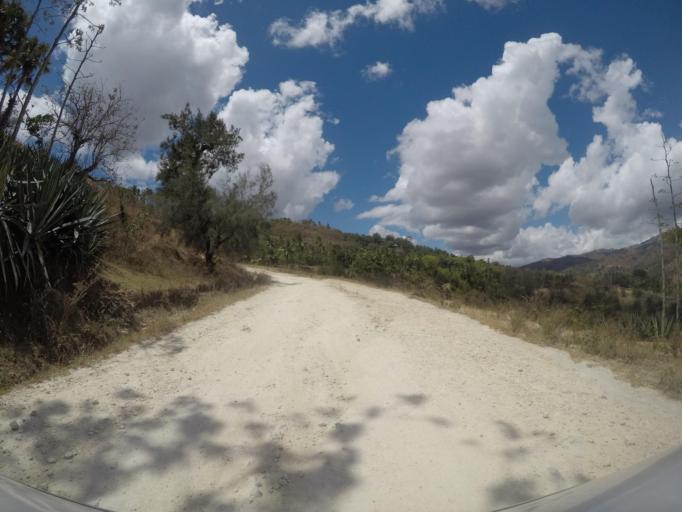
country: TL
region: Baucau
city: Baucau
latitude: -8.4875
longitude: 126.6431
